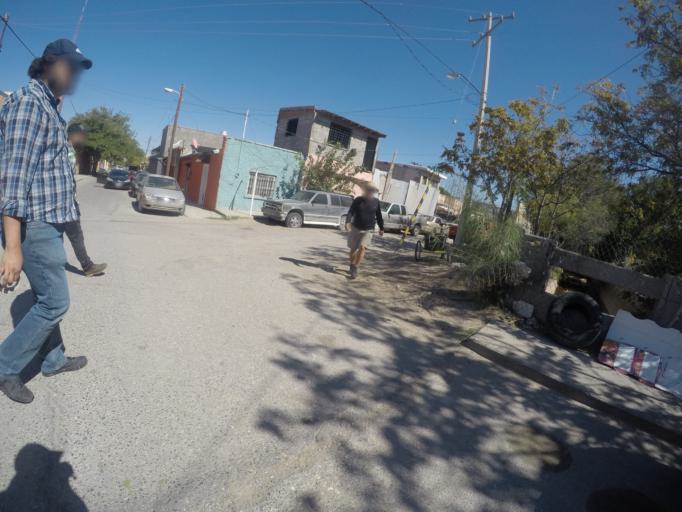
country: MX
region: Chihuahua
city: Ciudad Juarez
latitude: 31.7390
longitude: -106.4756
